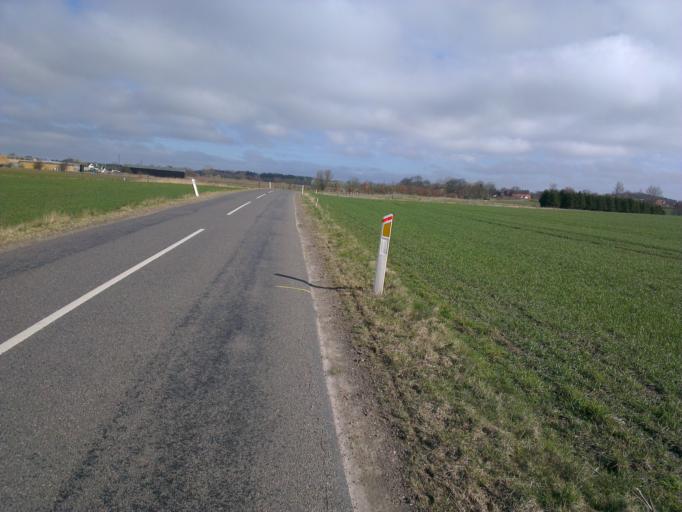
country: DK
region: Capital Region
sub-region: Hillerod Kommune
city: Skaevinge
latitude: 55.8783
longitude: 12.1218
